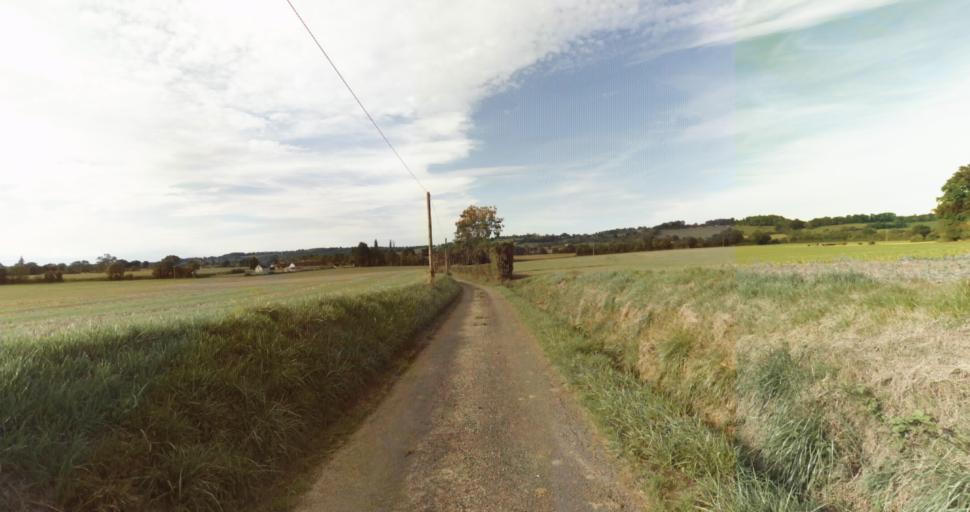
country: FR
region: Lower Normandy
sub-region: Departement de l'Orne
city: Gace
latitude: 48.7097
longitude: 0.2774
